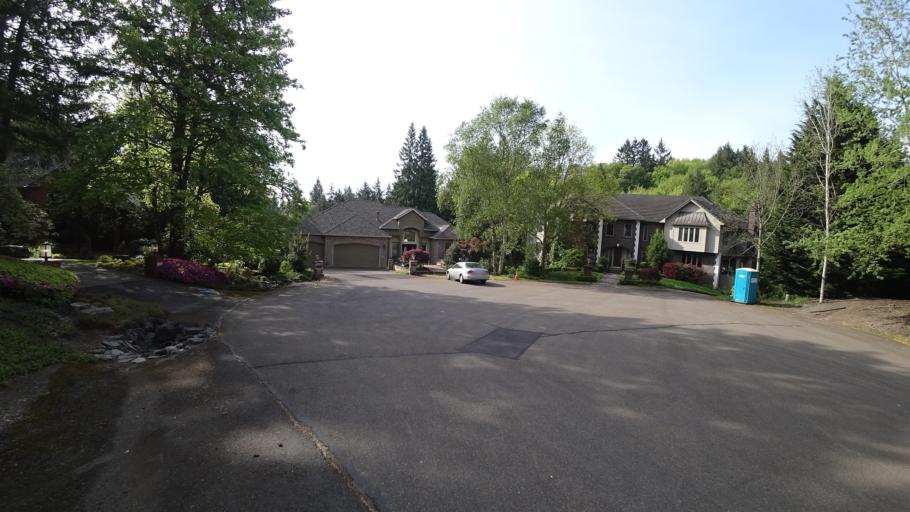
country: US
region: Oregon
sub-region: Washington County
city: Aloha
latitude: 45.4442
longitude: -122.8481
